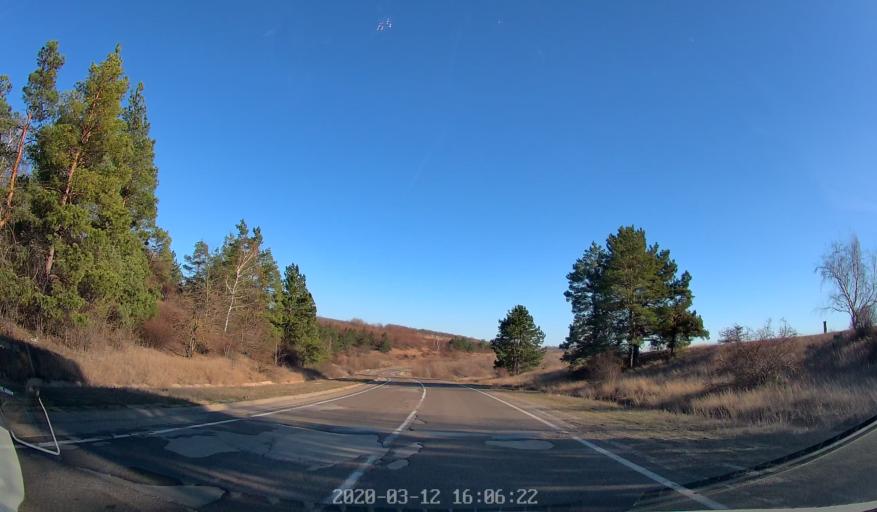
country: MD
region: Anenii Noi
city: Anenii Noi
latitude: 46.9935
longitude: 29.1893
